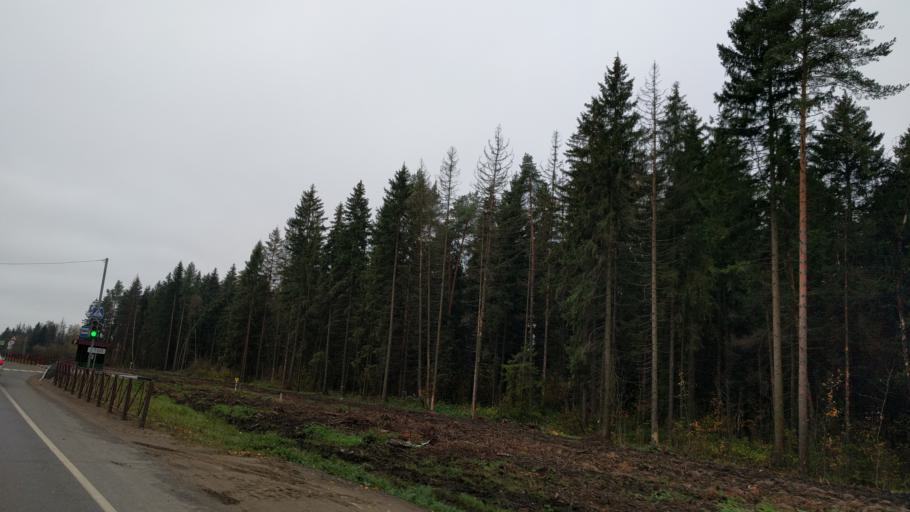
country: RU
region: Moskovskaya
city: Golitsyno
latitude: 55.5822
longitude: 37.0010
